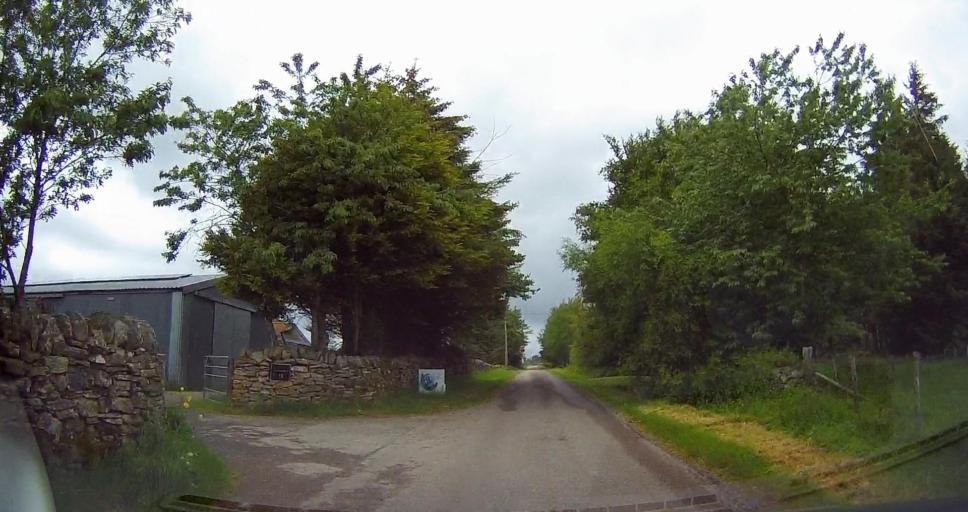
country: GB
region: Scotland
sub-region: Highland
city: Alness
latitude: 58.0754
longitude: -4.4410
